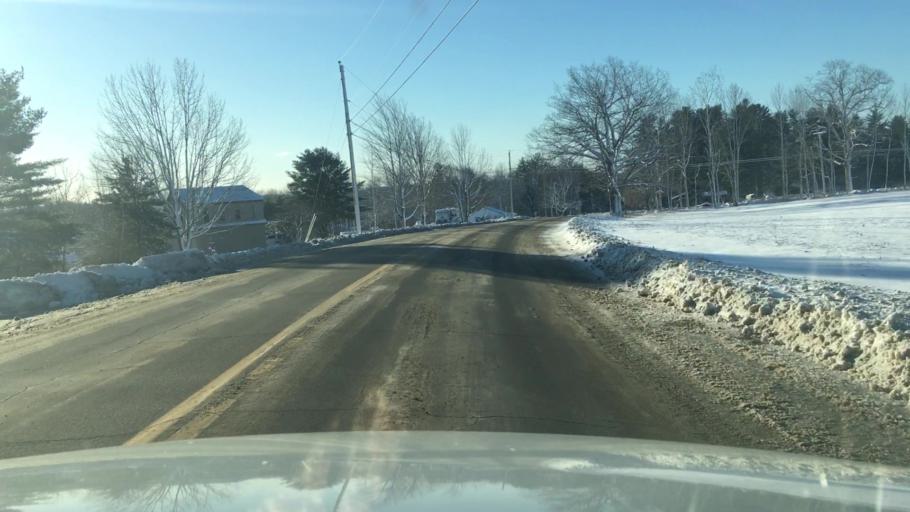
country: US
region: Maine
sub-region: Kennebec County
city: Readfield
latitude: 44.4204
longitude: -69.9287
